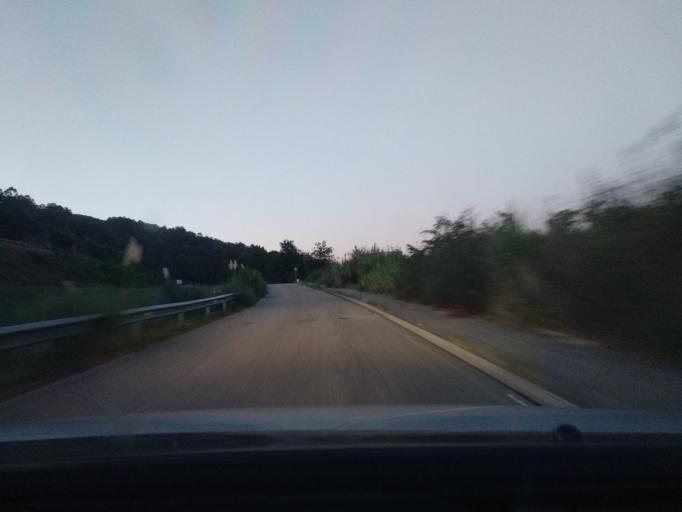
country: ES
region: Galicia
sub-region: Provincia de Pontevedra
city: Moana
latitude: 42.2862
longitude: -8.7534
